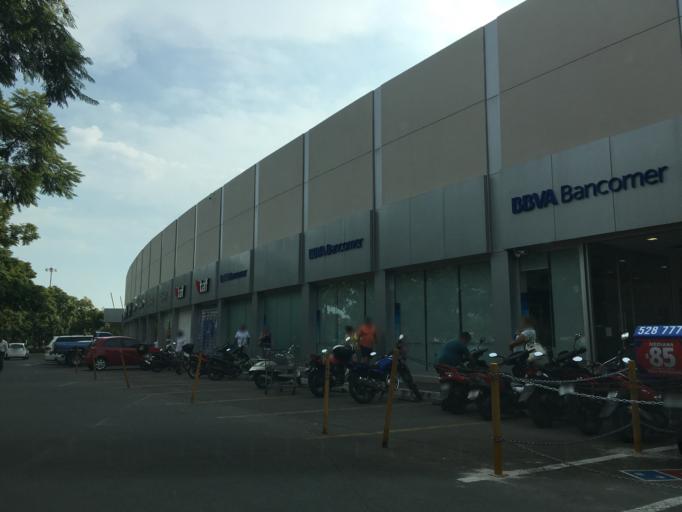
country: MX
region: Michoacan
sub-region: Uruapan
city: Uruapan
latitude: 19.4249
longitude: -102.0377
